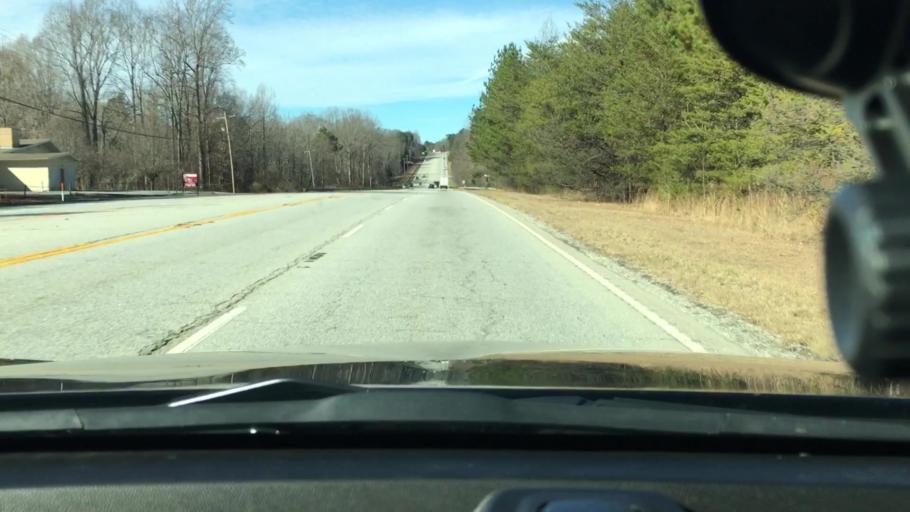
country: US
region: South Carolina
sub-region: Spartanburg County
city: Pacolet
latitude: 34.9169
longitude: -81.8146
